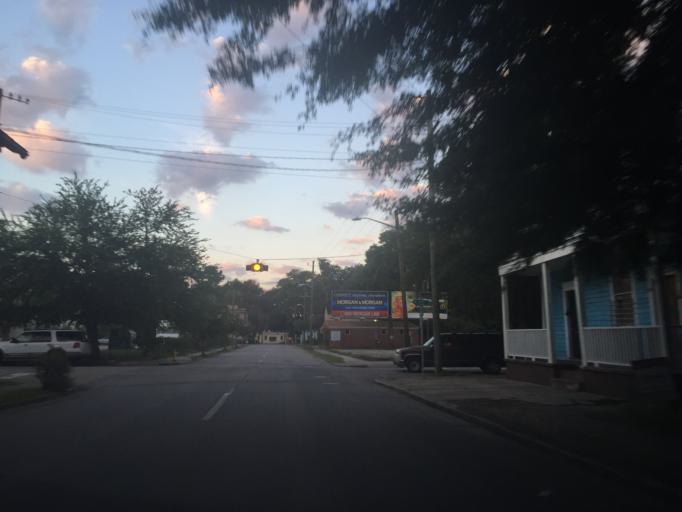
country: US
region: Georgia
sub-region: Chatham County
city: Savannah
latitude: 32.0551
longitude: -81.1021
